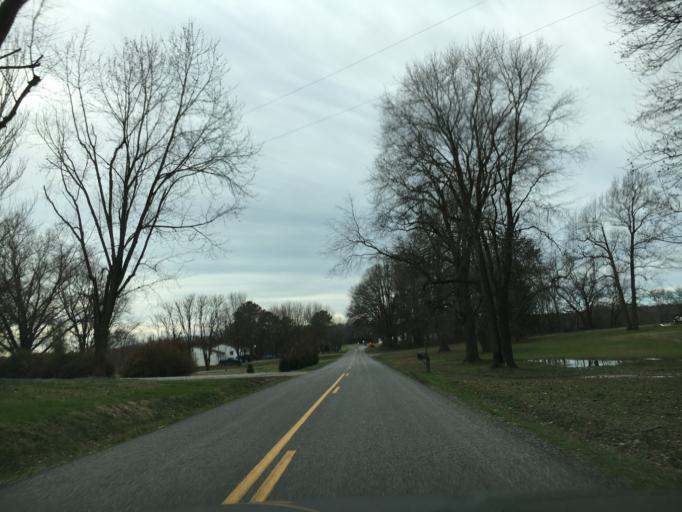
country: US
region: Virginia
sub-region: Amelia County
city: Amelia Court House
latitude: 37.4416
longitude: -78.0174
